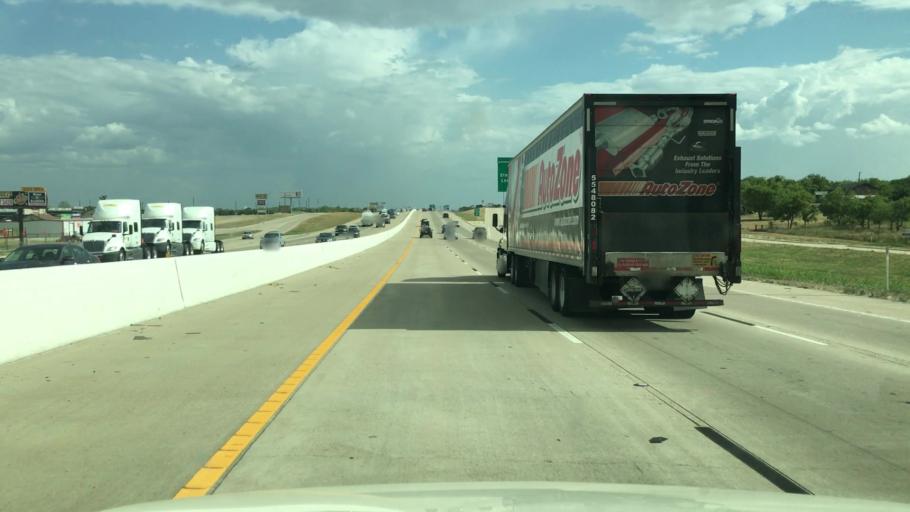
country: US
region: Texas
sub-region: McLennan County
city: Northcrest
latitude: 31.6853
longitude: -97.1000
